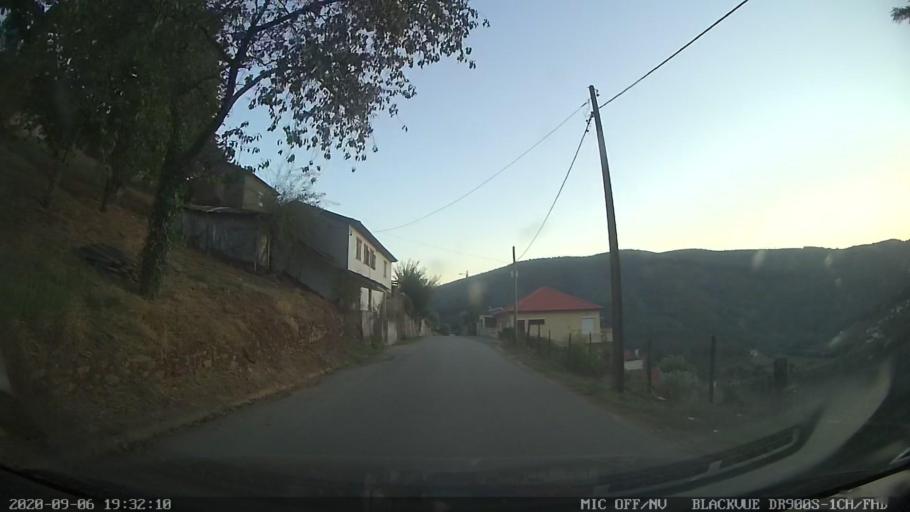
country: PT
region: Vila Real
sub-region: Mesao Frio
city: Mesao Frio
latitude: 41.1802
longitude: -7.9016
